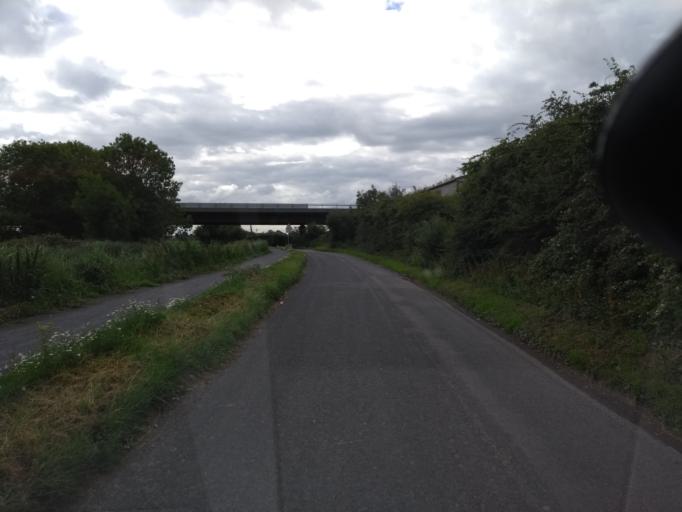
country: GB
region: England
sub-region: Somerset
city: Bridgwater
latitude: 51.1109
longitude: -2.9863
